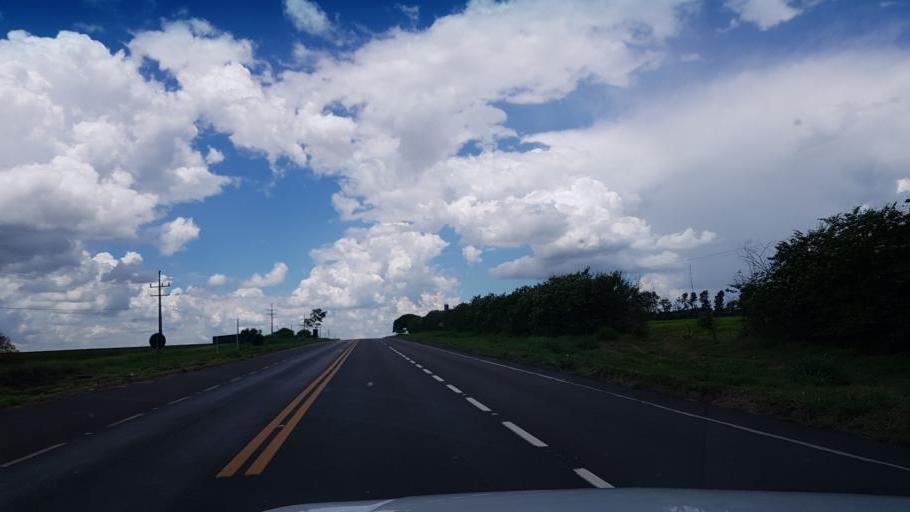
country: BR
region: Sao Paulo
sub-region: Paraguacu Paulista
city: Paraguacu Paulista
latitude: -22.3655
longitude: -50.6294
